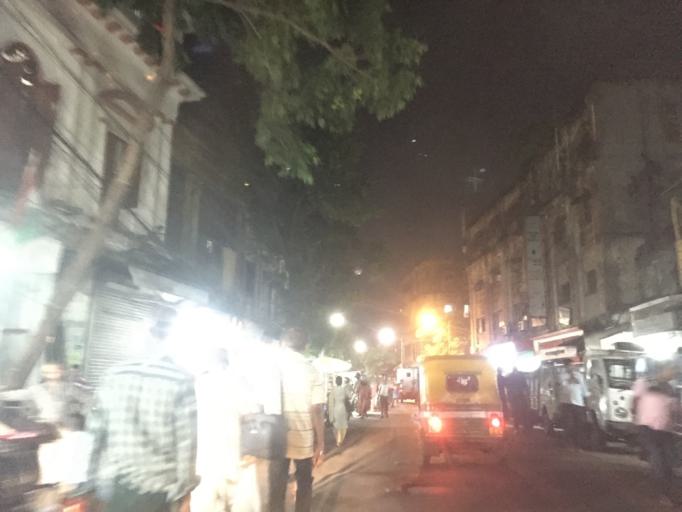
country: IN
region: West Bengal
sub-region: Kolkata
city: Bara Bazar
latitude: 22.5621
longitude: 88.3553
